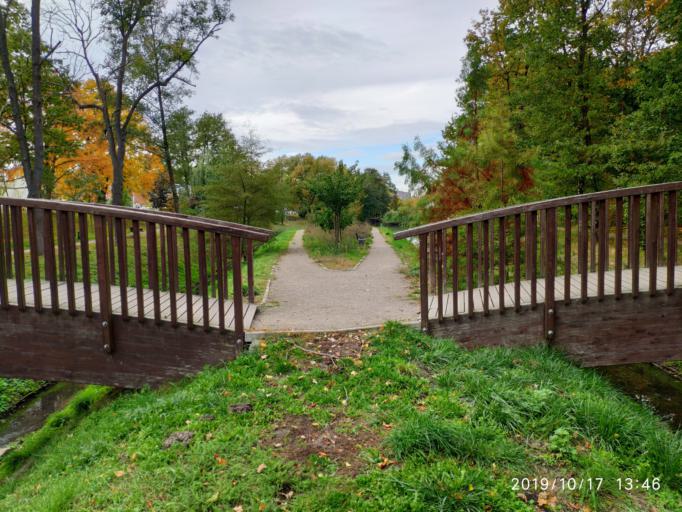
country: PL
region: Lubusz
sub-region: Zielona Gora
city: Zielona Gora
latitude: 51.9498
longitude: 15.5268
